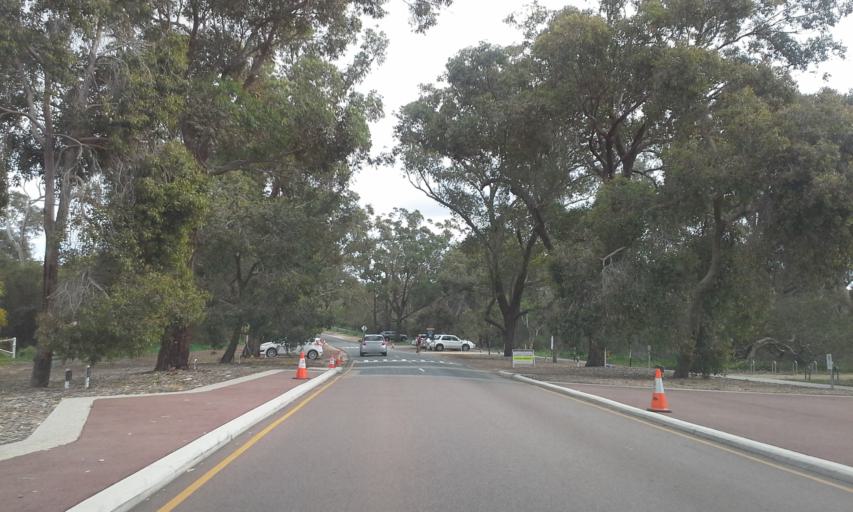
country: AU
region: Western Australia
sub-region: City of Perth
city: West Perth
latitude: -31.9588
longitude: 115.8396
